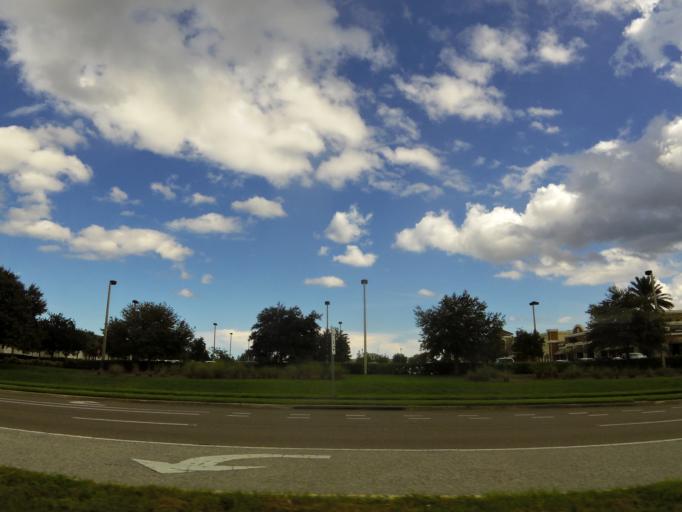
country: US
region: Florida
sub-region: Clay County
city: Green Cove Springs
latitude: 29.9622
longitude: -81.4924
